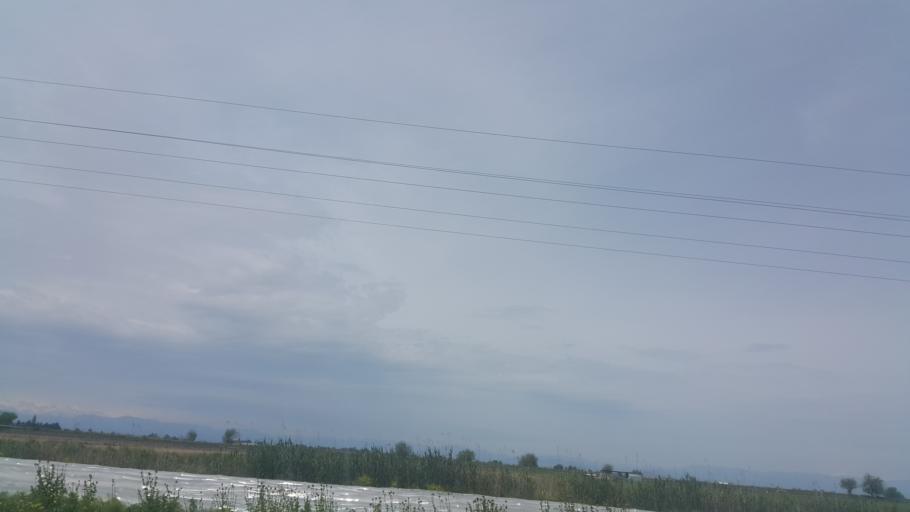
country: TR
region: Adana
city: Ceyhan
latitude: 37.0560
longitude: 35.8735
